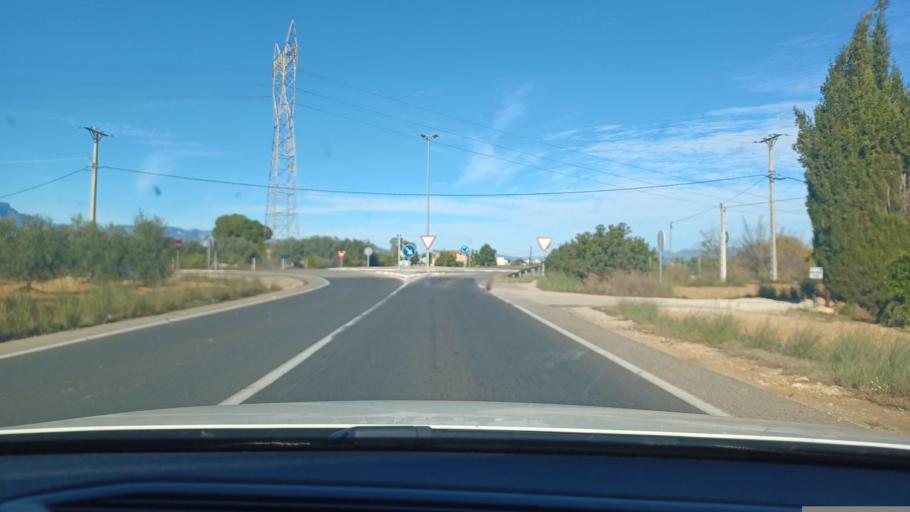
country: ES
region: Catalonia
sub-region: Provincia de Tarragona
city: Santa Barbara
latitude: 40.7062
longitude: 0.5032
